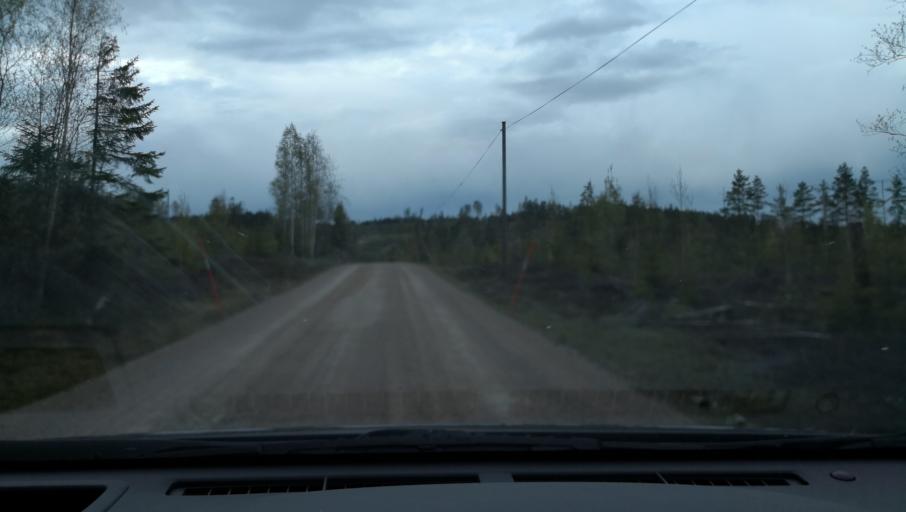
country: SE
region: Vaestmanland
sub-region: Fagersta Kommun
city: Fagersta
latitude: 60.1196
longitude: 15.7833
